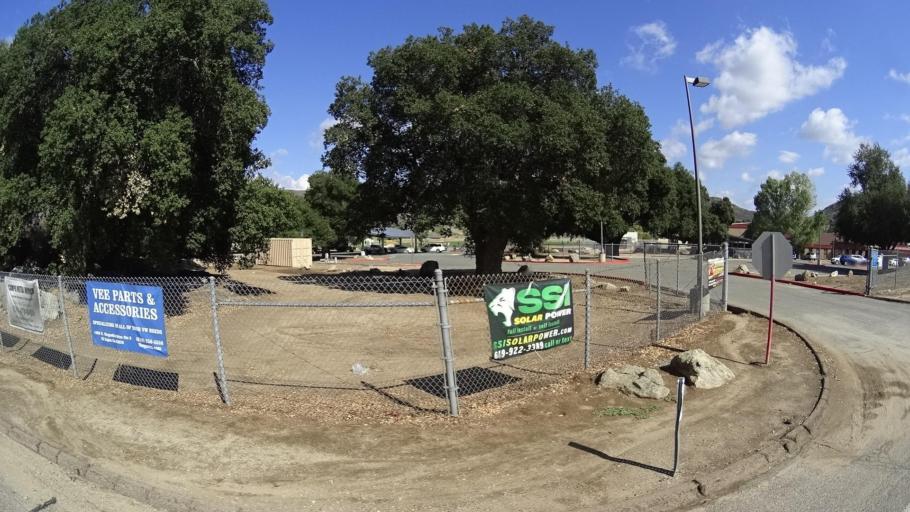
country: US
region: California
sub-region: San Diego County
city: Pine Valley
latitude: 32.7347
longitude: -116.4937
